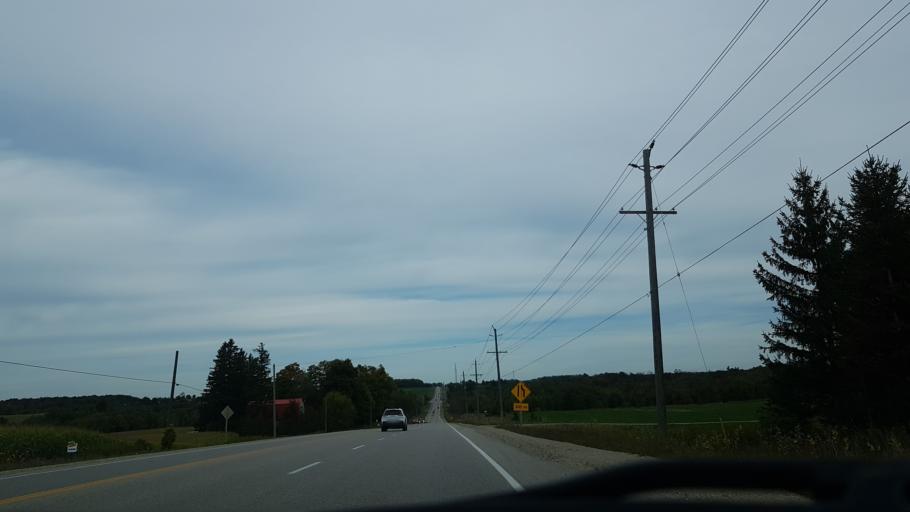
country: CA
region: Ontario
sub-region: Wellington County
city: Guelph
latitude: 43.6607
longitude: -80.1735
